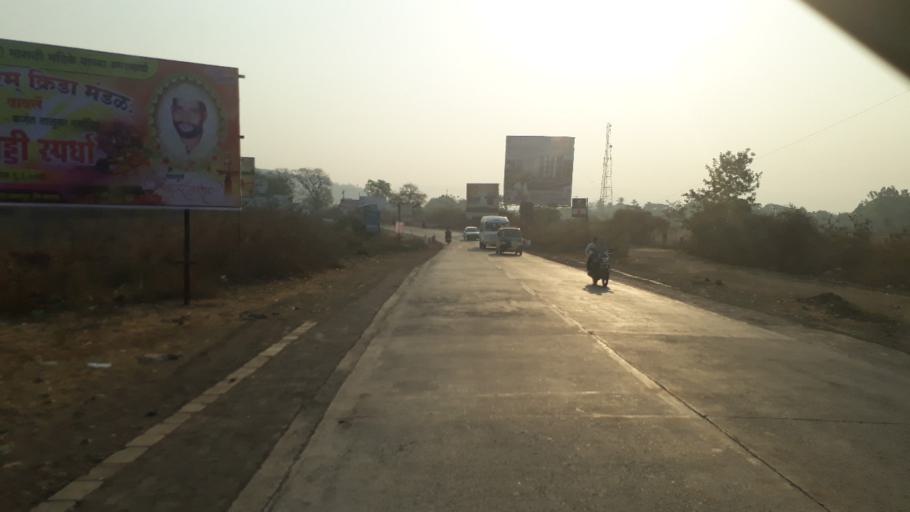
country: IN
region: Maharashtra
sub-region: Raigarh
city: Karjat
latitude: 18.9159
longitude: 73.2875
